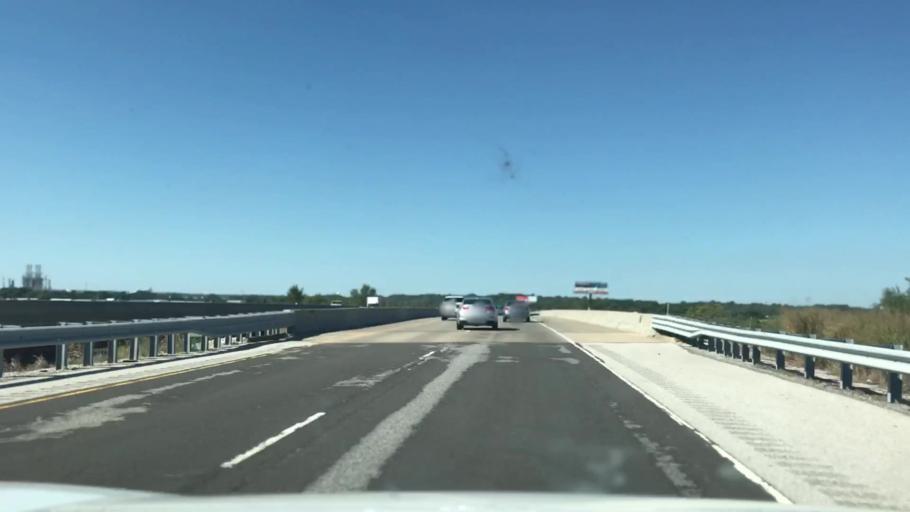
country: US
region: Illinois
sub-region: Madison County
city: South Roxana
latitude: 38.8167
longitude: -90.0422
